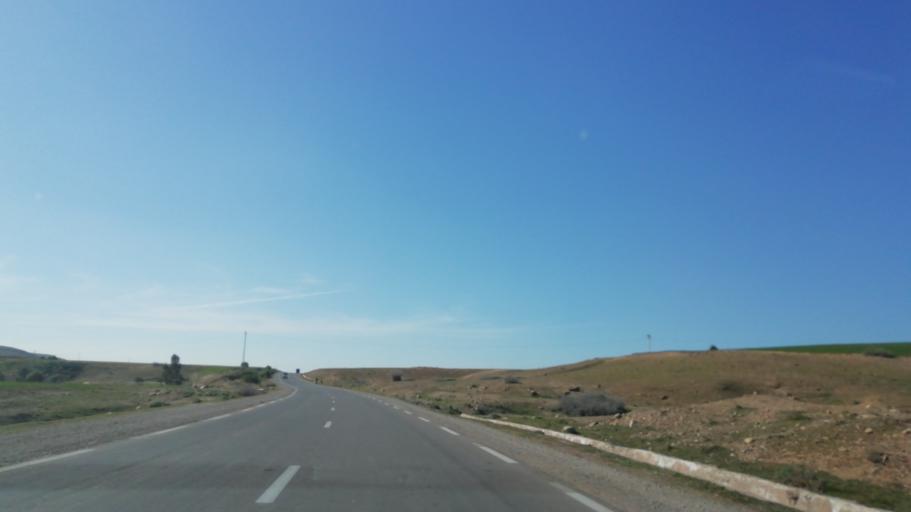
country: DZ
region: Mascara
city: Oued el Abtal
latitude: 35.4535
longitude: 0.7746
